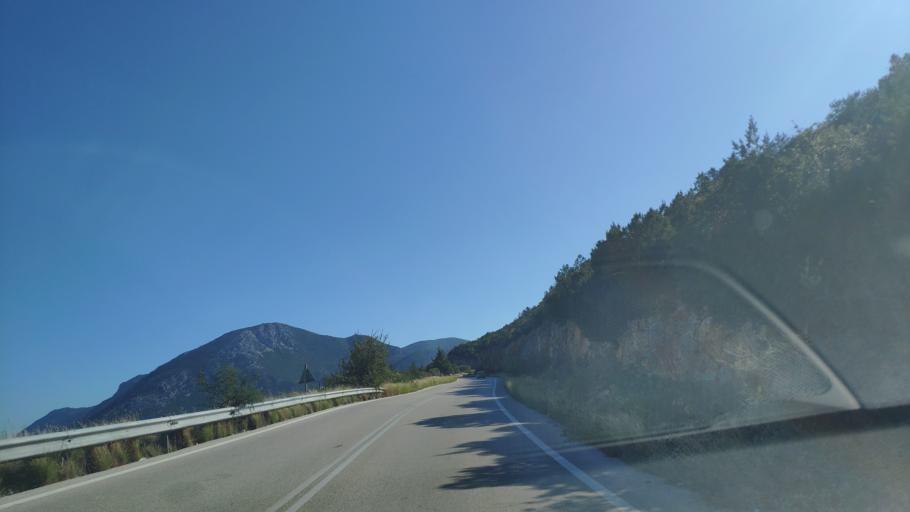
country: GR
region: Peloponnese
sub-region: Nomos Argolidos
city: Palaia Epidavros
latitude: 37.6279
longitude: 23.1433
